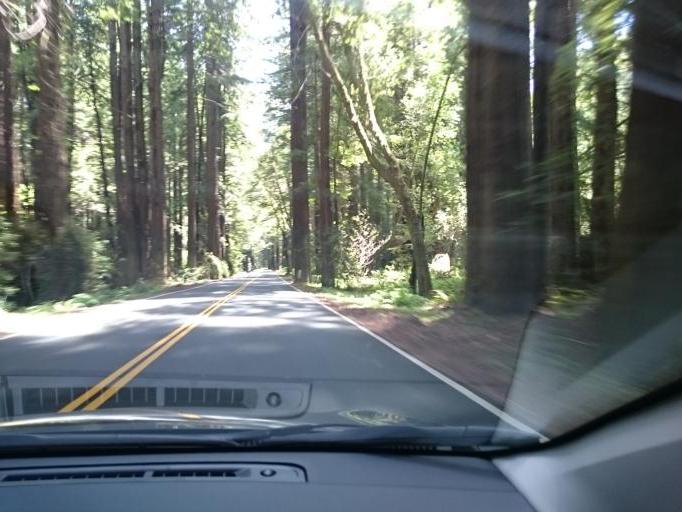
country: US
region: California
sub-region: Mendocino County
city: Boonville
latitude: 39.1575
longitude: -123.6313
